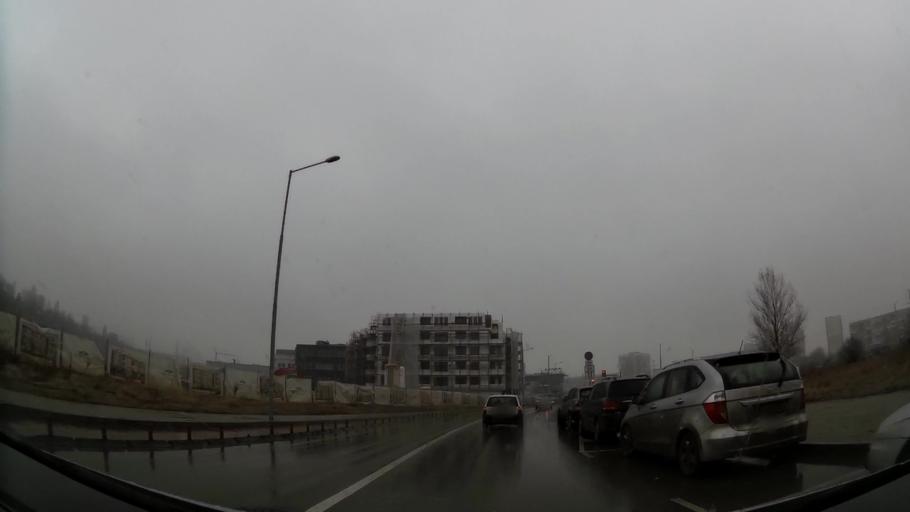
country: BG
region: Sofia-Capital
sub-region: Stolichna Obshtina
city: Sofia
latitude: 42.6565
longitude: 23.3942
